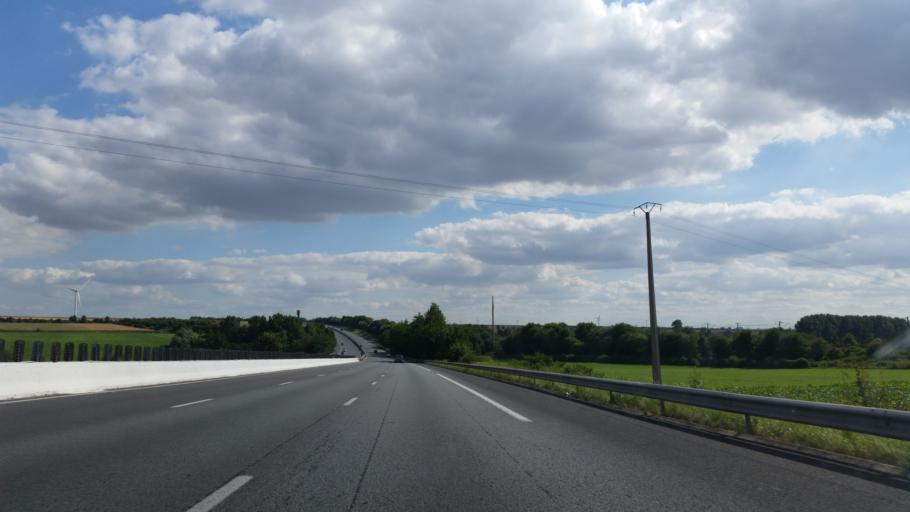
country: FR
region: Nord-Pas-de-Calais
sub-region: Departement du Pas-de-Calais
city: Croisilles
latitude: 50.2387
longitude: 2.8545
